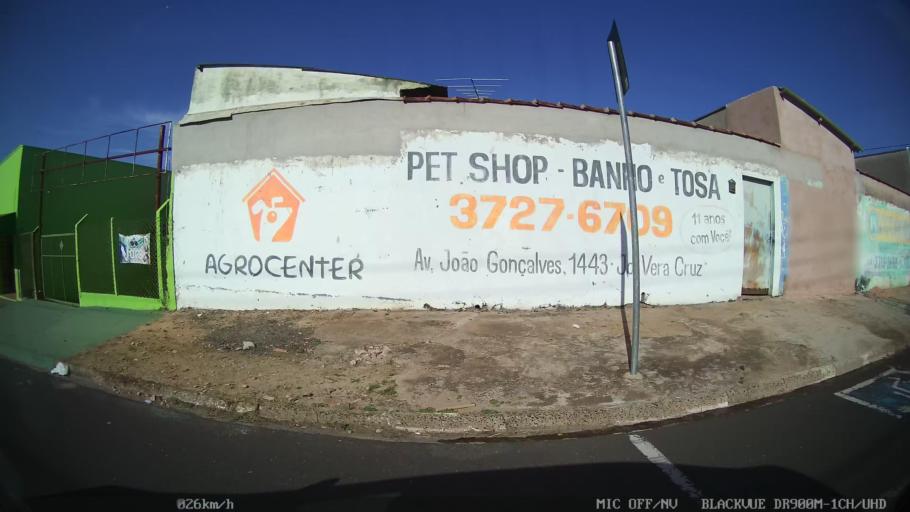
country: BR
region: Sao Paulo
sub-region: Franca
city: Franca
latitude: -20.4954
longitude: -47.4143
